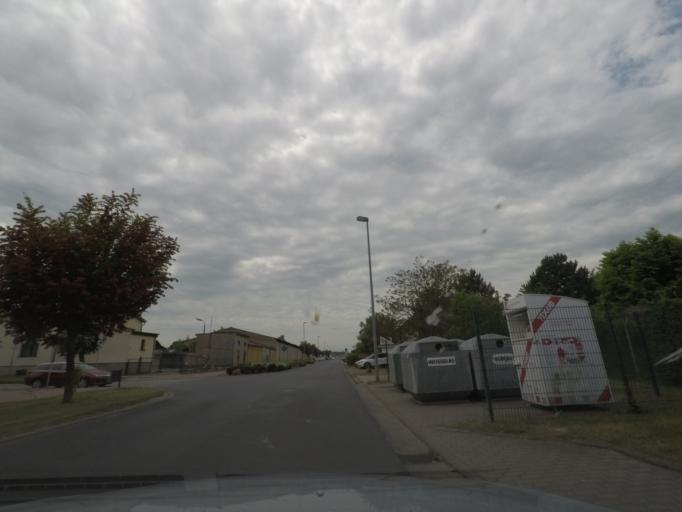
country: DE
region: Brandenburg
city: Prenzlau
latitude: 53.3259
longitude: 13.8721
